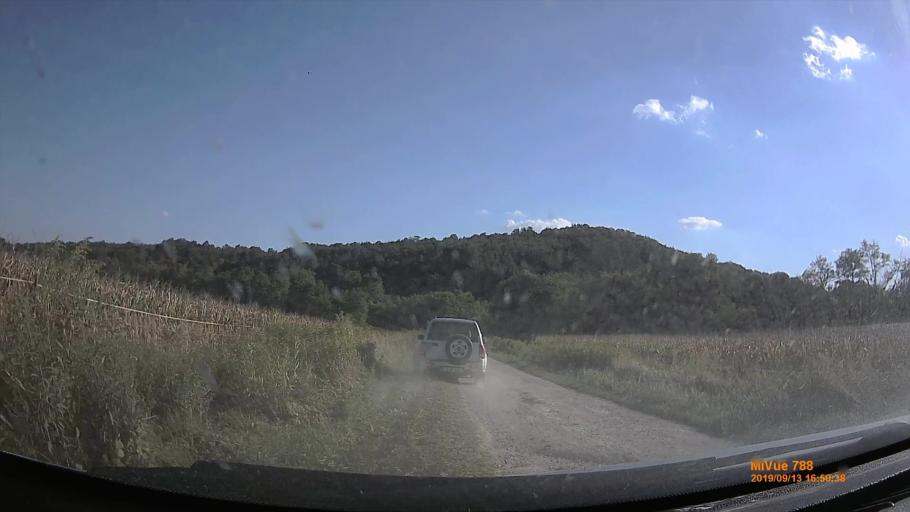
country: HU
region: Zala
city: Pacsa
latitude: 46.6062
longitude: 17.0657
